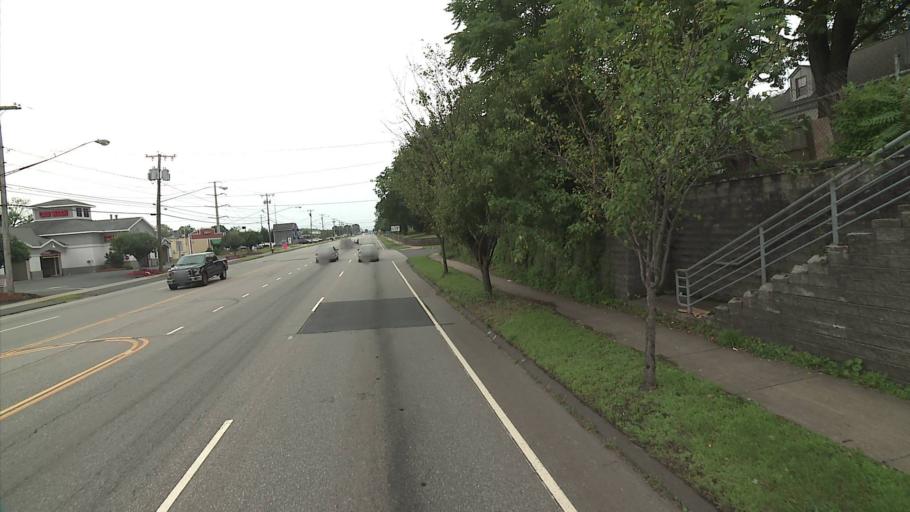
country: US
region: Connecticut
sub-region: Hartford County
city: Wethersfield
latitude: 41.7041
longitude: -72.6608
